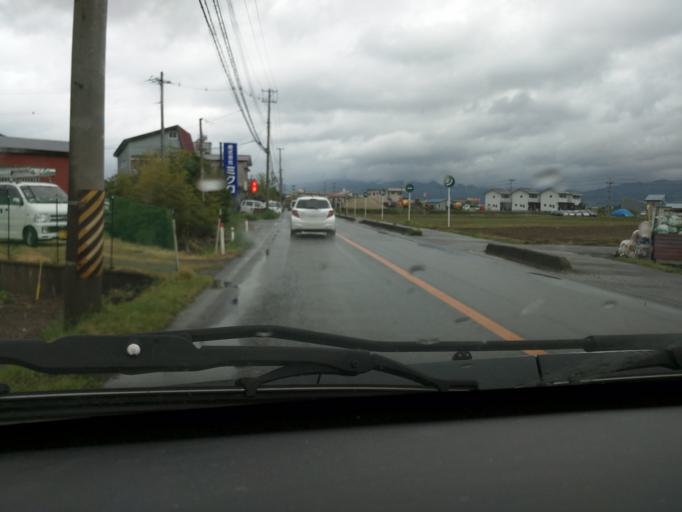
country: JP
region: Fukushima
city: Kitakata
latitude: 37.6289
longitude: 139.8719
